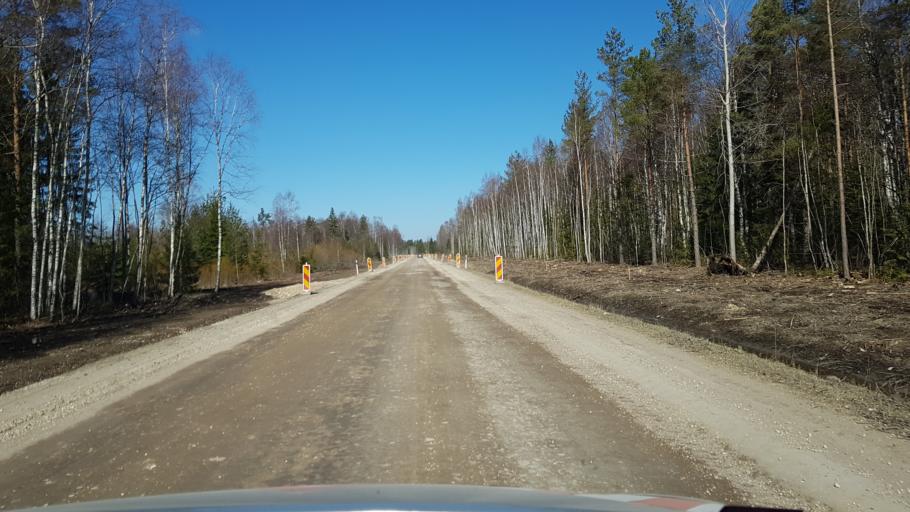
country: EE
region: Laeaene-Virumaa
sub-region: Vinni vald
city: Vinni
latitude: 59.0511
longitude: 26.6550
